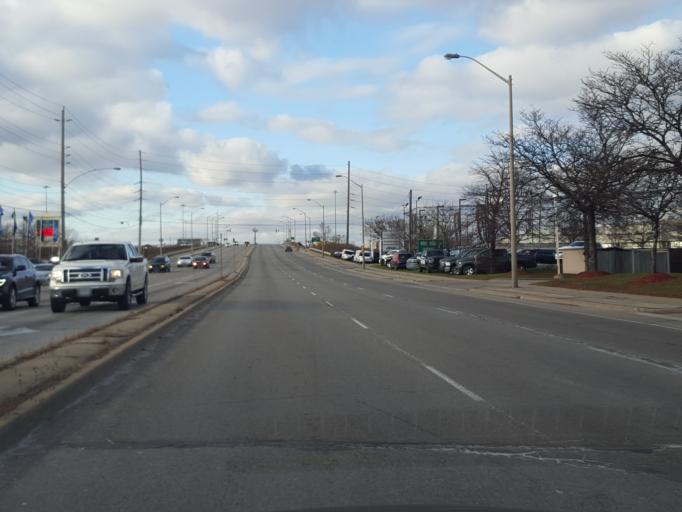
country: CA
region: Ontario
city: Burlington
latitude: 43.3631
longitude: -79.7835
